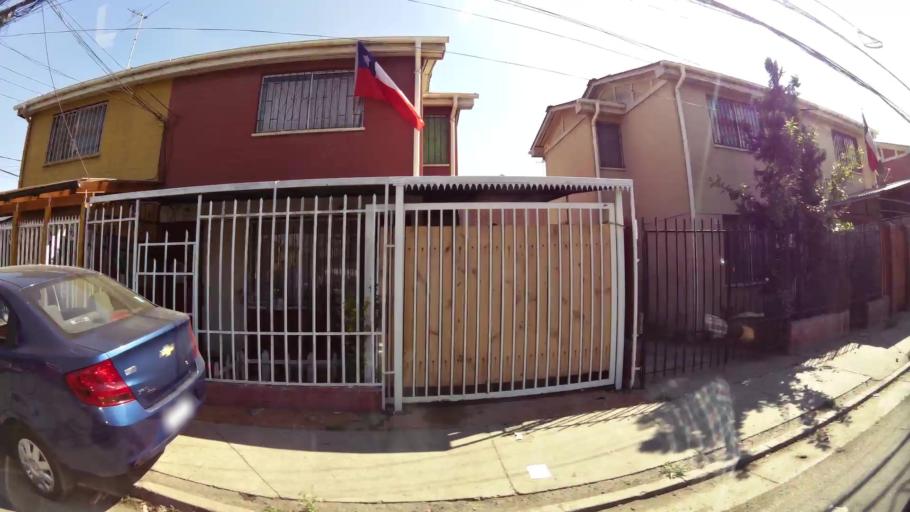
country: CL
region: Santiago Metropolitan
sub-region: Provincia de Santiago
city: Lo Prado
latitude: -33.3590
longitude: -70.7528
